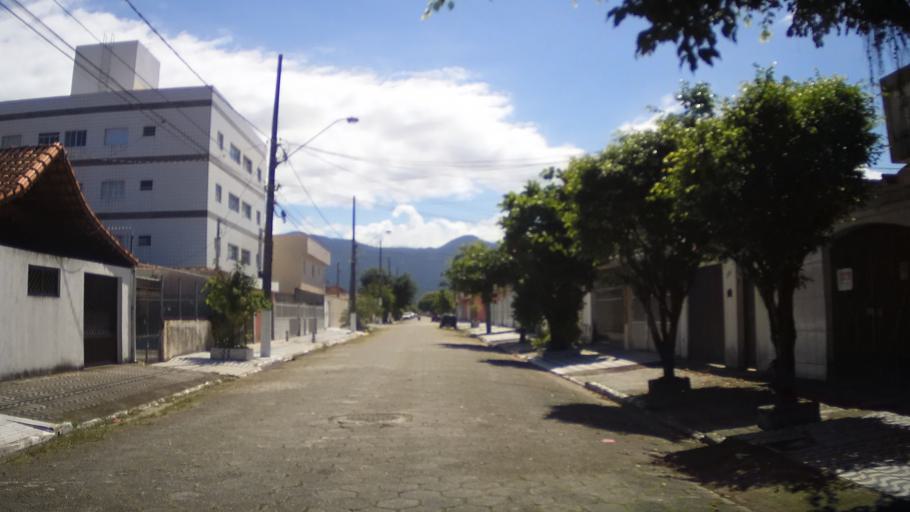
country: BR
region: Sao Paulo
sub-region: Praia Grande
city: Praia Grande
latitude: -24.0406
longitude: -46.5075
